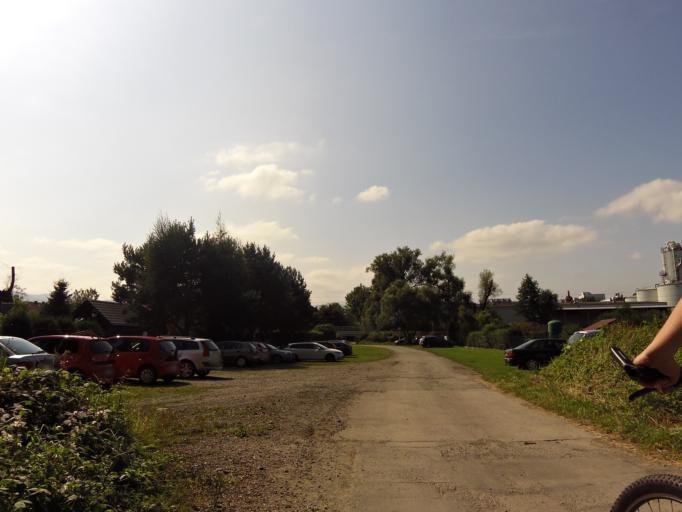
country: PL
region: Silesian Voivodeship
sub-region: Powiat zywiecki
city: Wieprz
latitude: 49.6607
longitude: 19.1787
